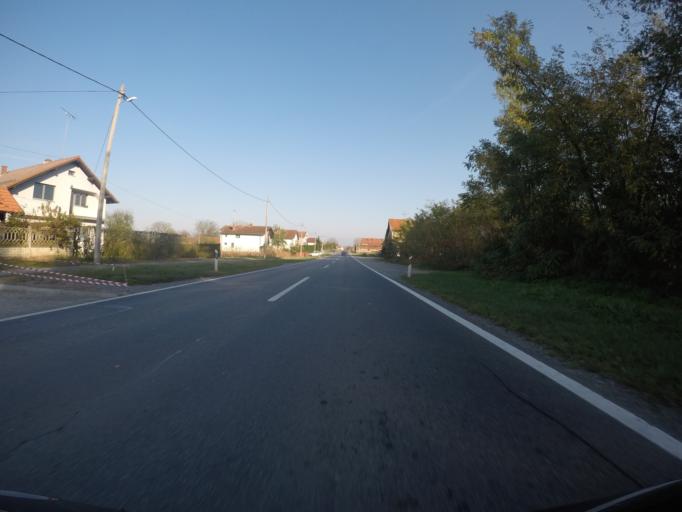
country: HR
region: Virovitick-Podravska
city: Pitomaca
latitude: 45.9688
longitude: 17.1904
